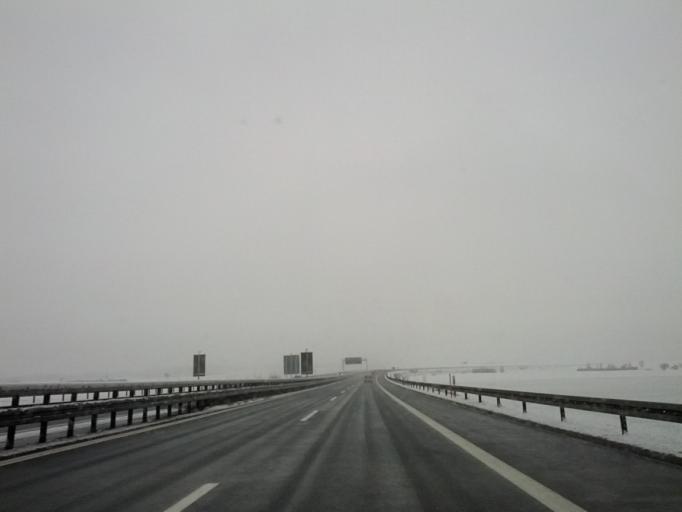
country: DE
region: Bavaria
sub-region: Regierungsbezirk Unterfranken
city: Geldersheim
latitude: 50.0260
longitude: 10.1486
